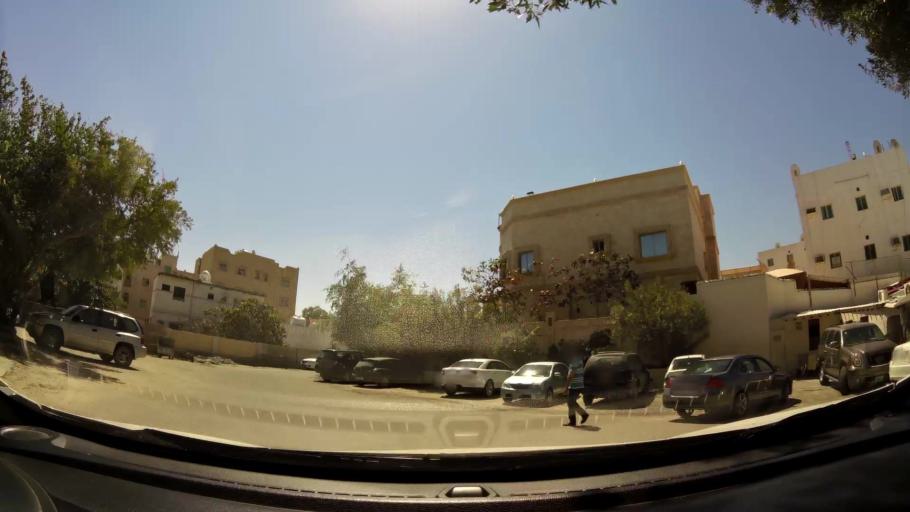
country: BH
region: Muharraq
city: Al Muharraq
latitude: 26.2839
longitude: 50.6355
